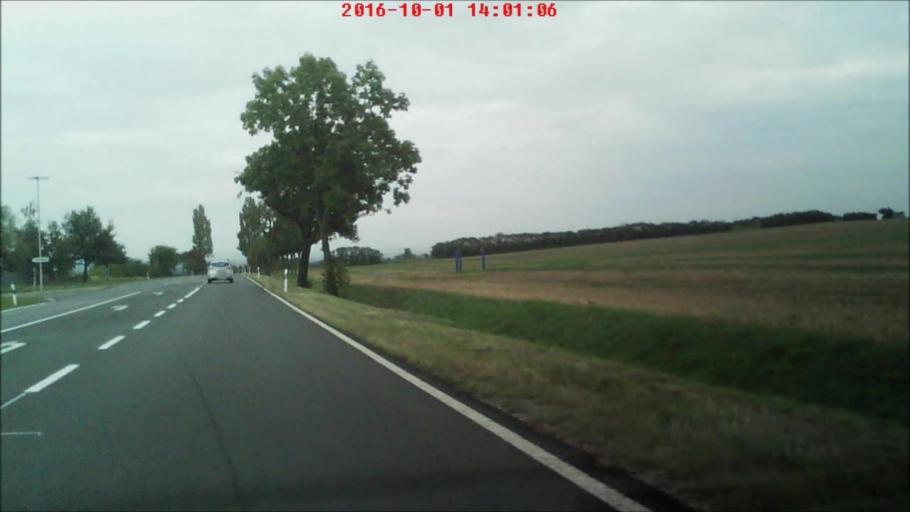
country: DE
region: Thuringia
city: Umpferstedt
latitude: 50.9812
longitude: 11.4208
